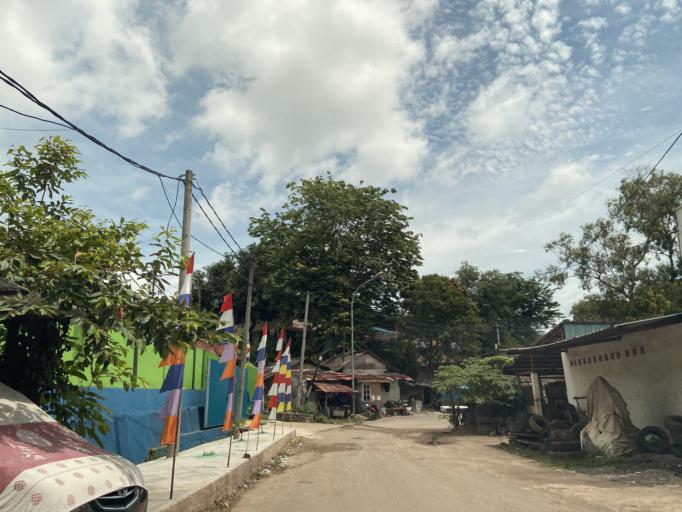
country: SG
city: Singapore
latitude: 1.1607
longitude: 104.0062
